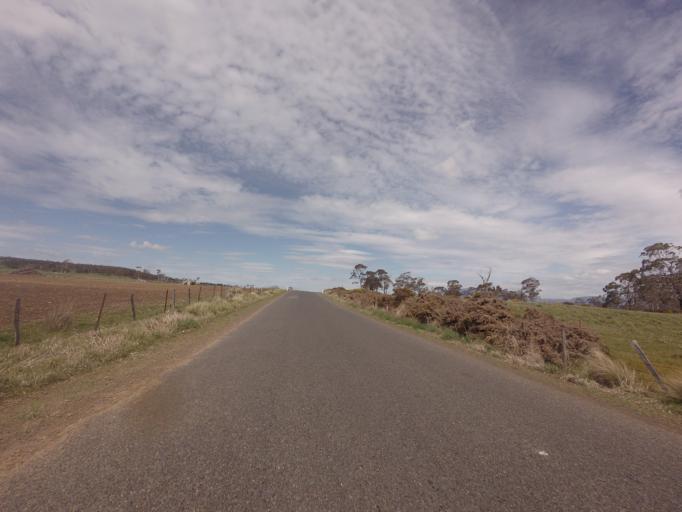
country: AU
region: Tasmania
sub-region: Northern Midlands
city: Longford
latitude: -41.7396
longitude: 147.2021
